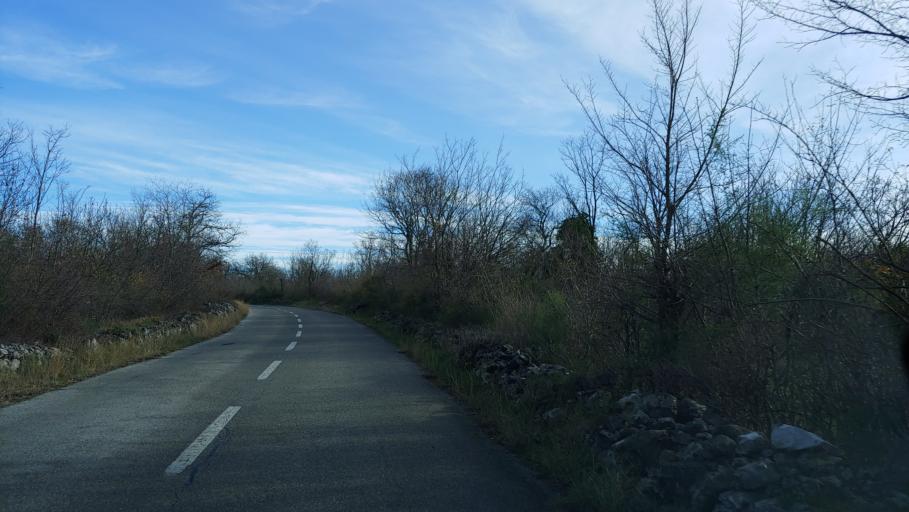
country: IT
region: Friuli Venezia Giulia
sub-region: Provincia di Trieste
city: Duino
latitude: 45.8122
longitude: 13.6172
